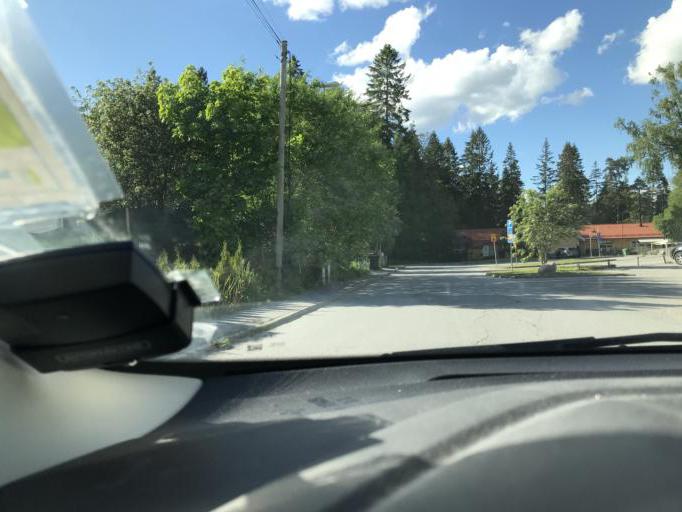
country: SE
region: Stockholm
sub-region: Botkyrka Kommun
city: Tumba
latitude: 59.1983
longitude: 17.8227
